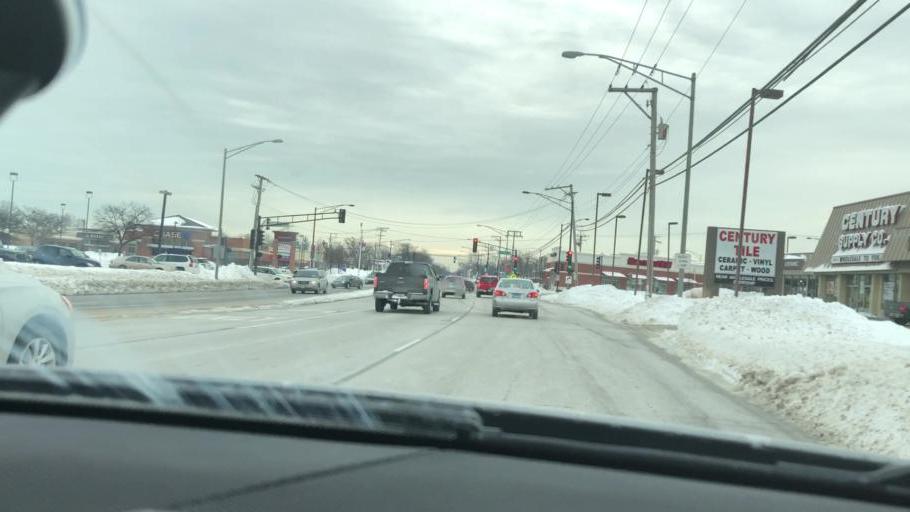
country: US
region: Illinois
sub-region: Cook County
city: Mount Prospect
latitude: 42.0674
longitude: -87.9231
